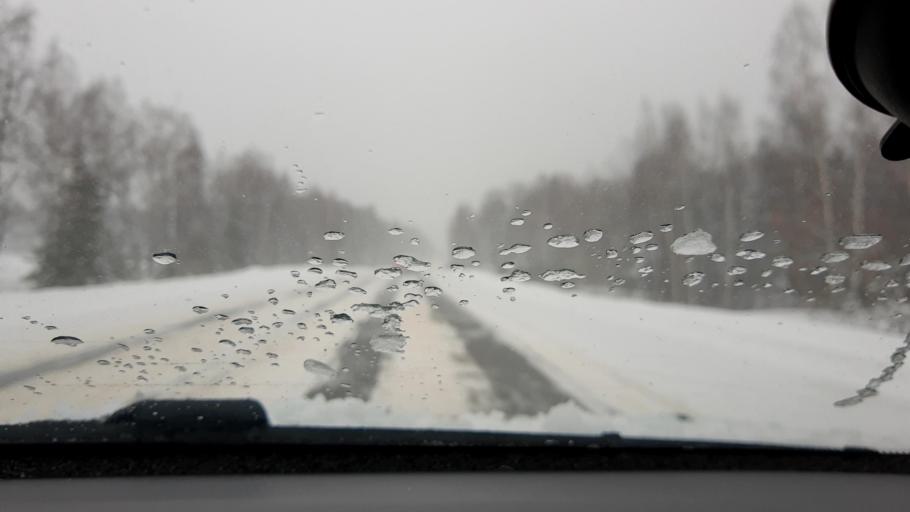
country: RU
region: Nizjnij Novgorod
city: Purekh
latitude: 56.6306
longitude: 43.1855
